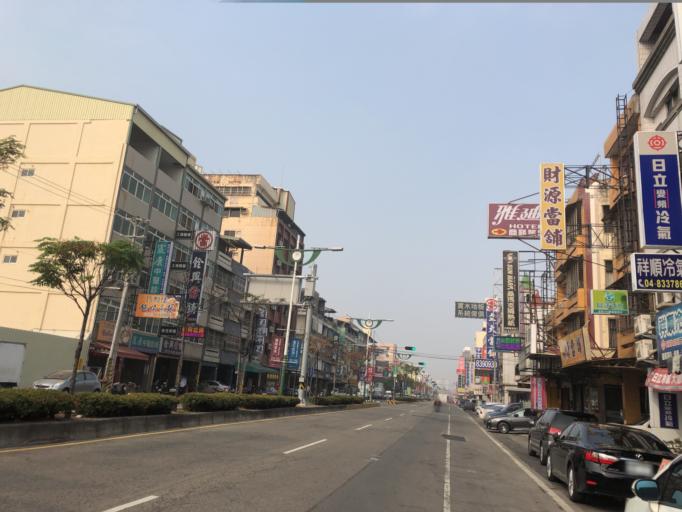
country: TW
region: Taiwan
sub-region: Nantou
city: Nantou
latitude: 23.9572
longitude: 120.5668
